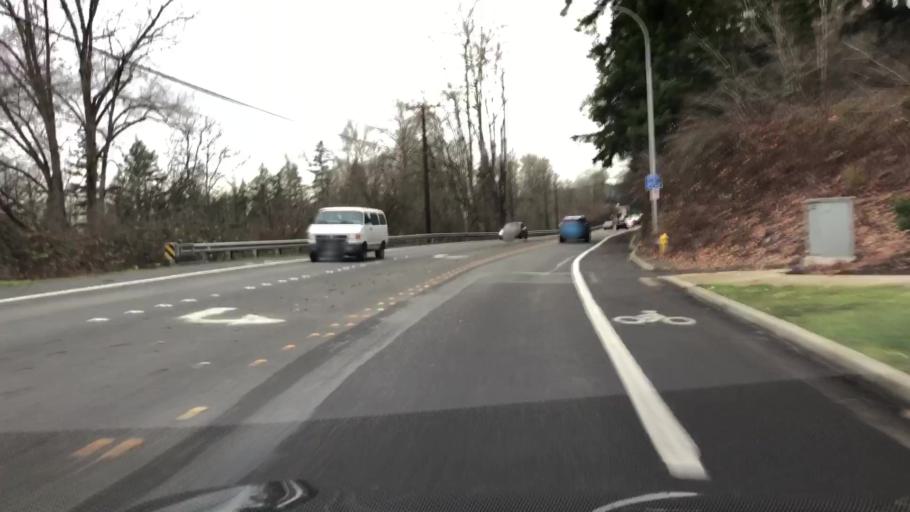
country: US
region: Washington
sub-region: King County
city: Sammamish
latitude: 47.6565
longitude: -122.0937
